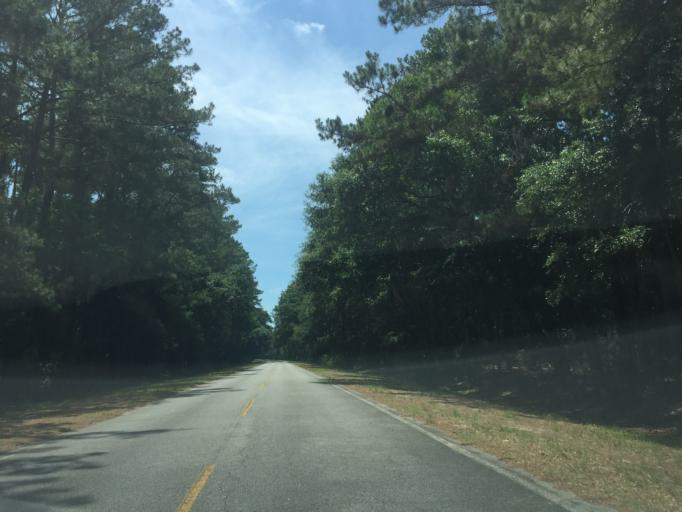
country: US
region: Georgia
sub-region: Chatham County
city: Skidaway Island
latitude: 31.9629
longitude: -81.0193
